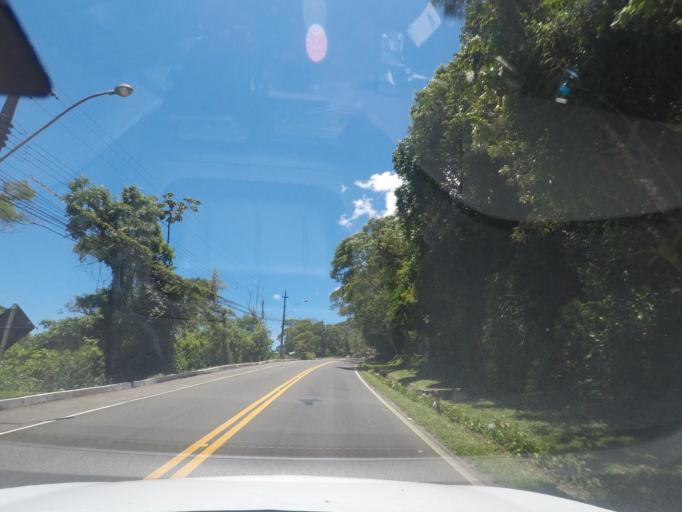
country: BR
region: Rio de Janeiro
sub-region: Teresopolis
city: Teresopolis
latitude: -22.4581
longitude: -42.9858
